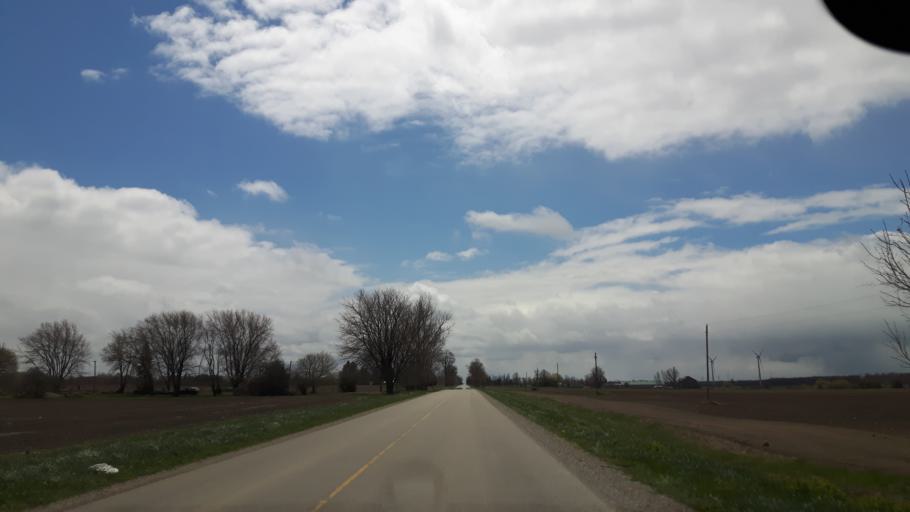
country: CA
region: Ontario
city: Bluewater
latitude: 43.5199
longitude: -81.6707
